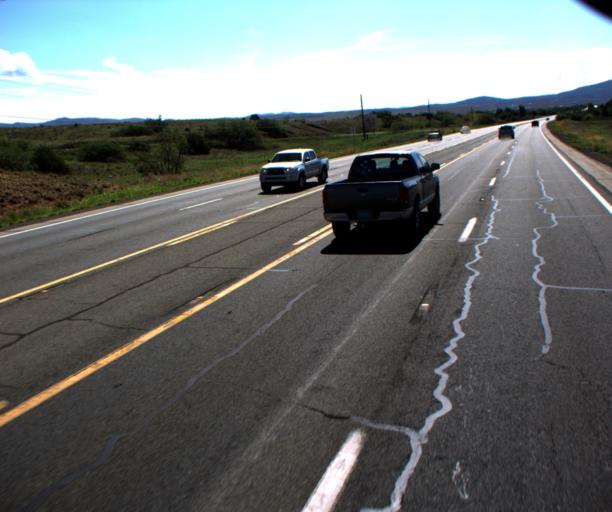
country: US
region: Arizona
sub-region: Yavapai County
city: Prescott Valley
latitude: 34.5726
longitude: -112.2779
